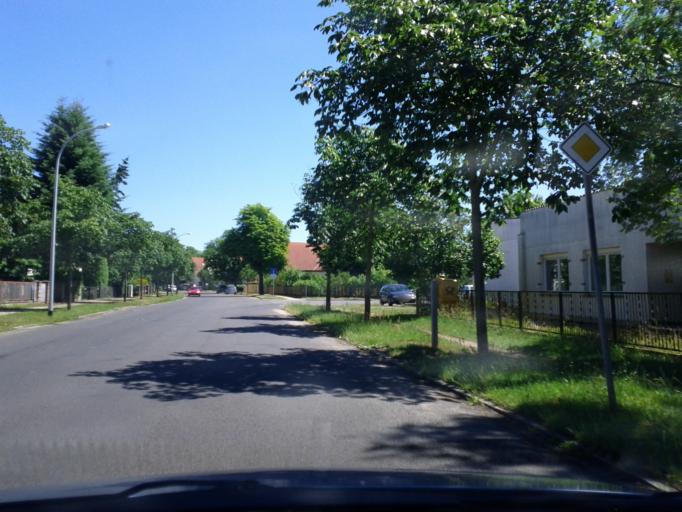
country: DE
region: Brandenburg
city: Furstenwalde
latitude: 52.3542
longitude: 14.0576
